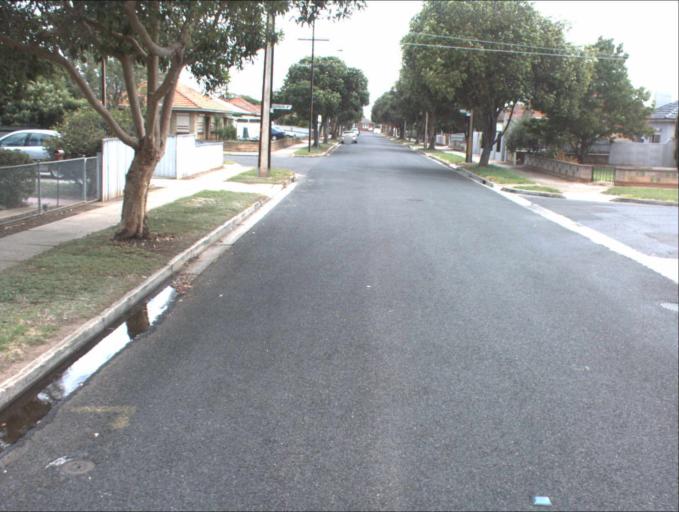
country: AU
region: South Australia
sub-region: Charles Sturt
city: Woodville
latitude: -34.8827
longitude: 138.5639
